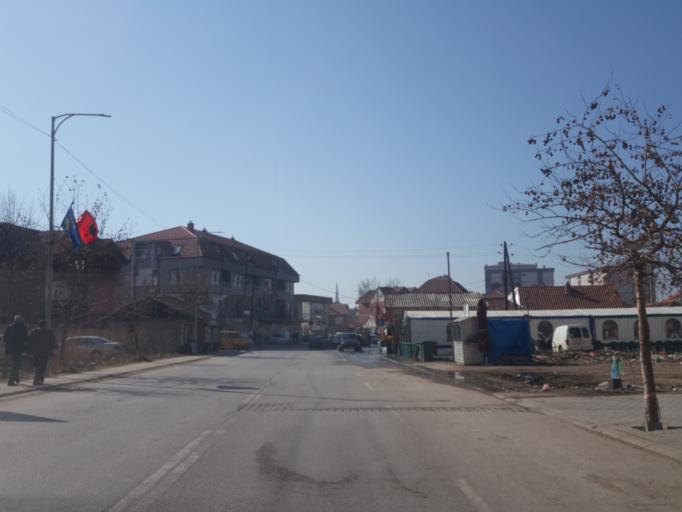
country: XK
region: Mitrovica
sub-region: Vushtrri
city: Vushtrri
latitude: 42.8252
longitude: 20.9686
